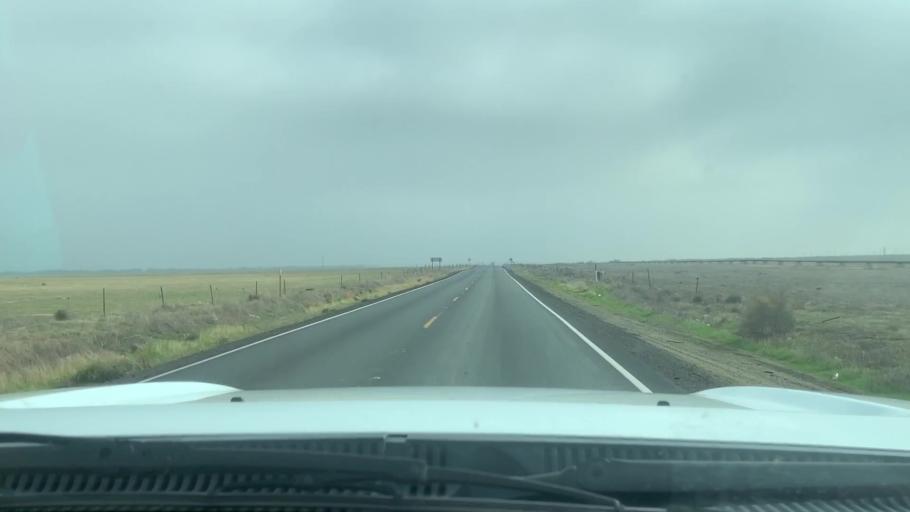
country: US
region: California
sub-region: Kern County
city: Lost Hills
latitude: 35.5569
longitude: -119.7963
